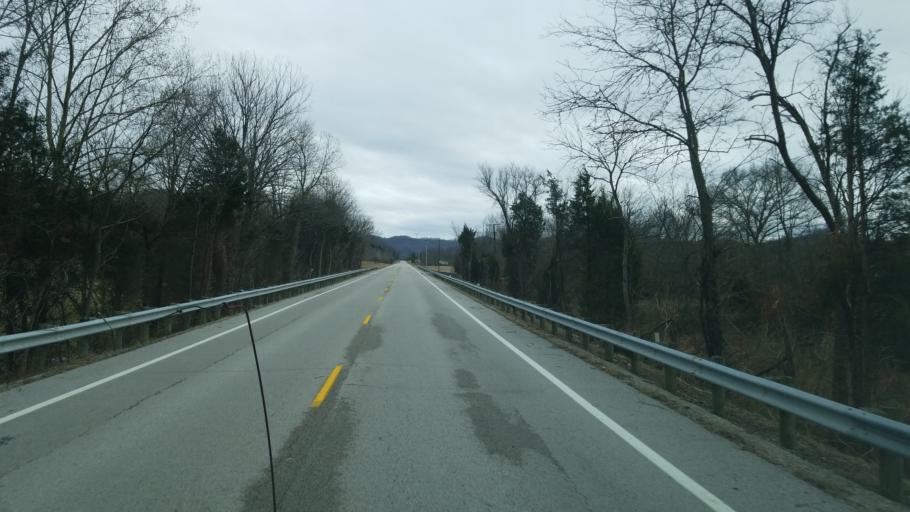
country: US
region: Ohio
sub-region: Adams County
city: West Union
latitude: 38.6813
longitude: -83.4555
